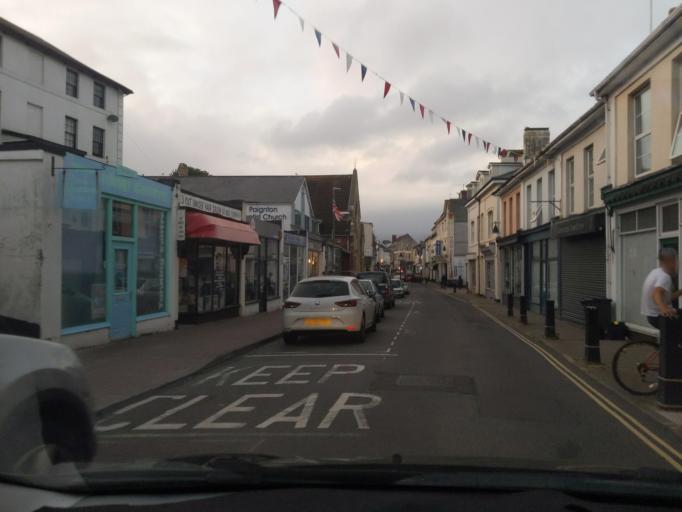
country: GB
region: England
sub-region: Borough of Torbay
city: Paignton
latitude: 50.4336
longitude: -3.5720
